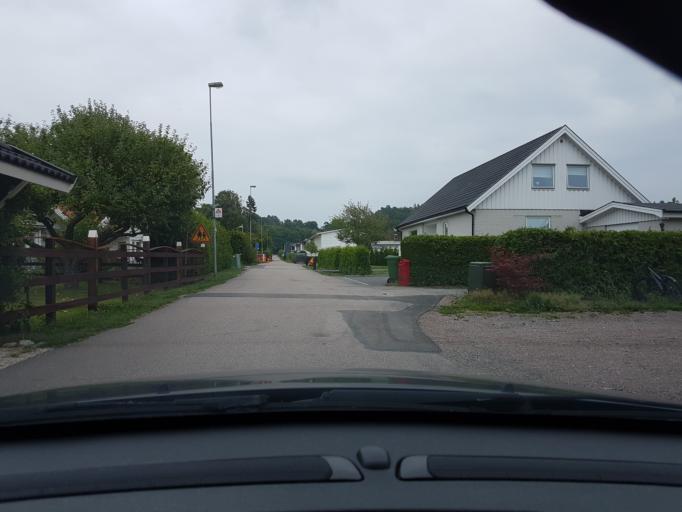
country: SE
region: Vaestra Goetaland
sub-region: Ale Kommun
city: Nodinge-Nol
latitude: 57.8893
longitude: 12.0527
